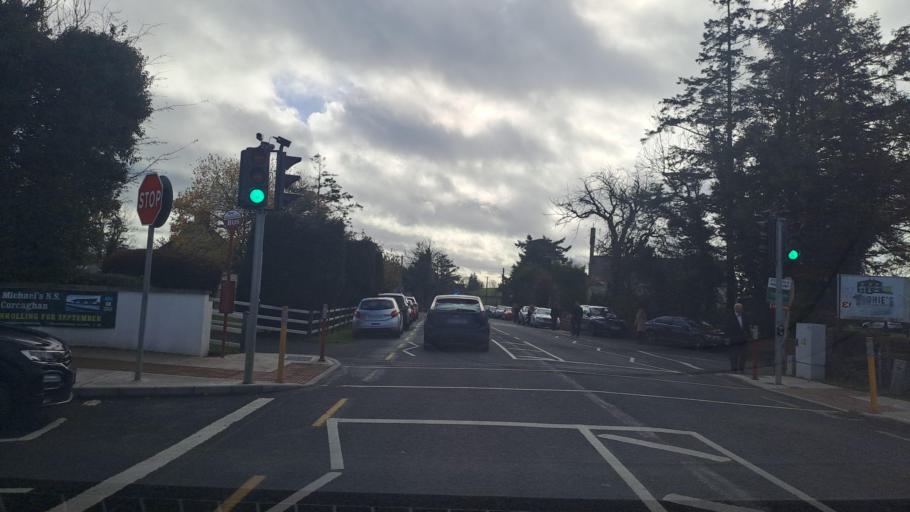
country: IE
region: Ulster
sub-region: County Monaghan
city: Monaghan
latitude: 54.1909
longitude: -6.9905
